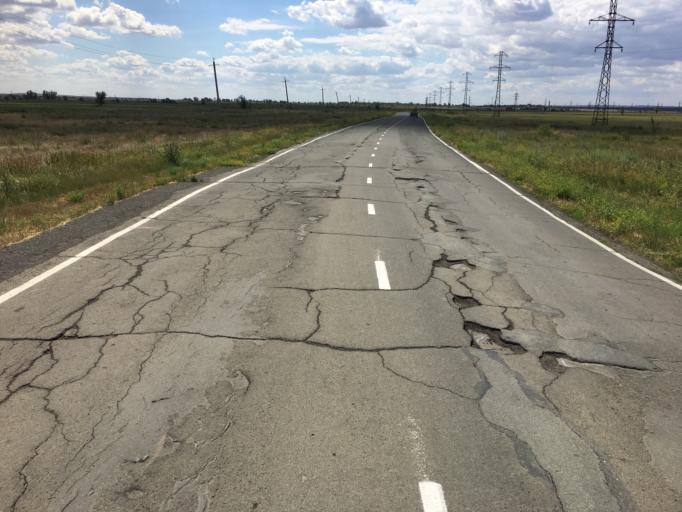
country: RU
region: Orenburg
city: Novotroitsk
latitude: 51.1559
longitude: 58.3405
